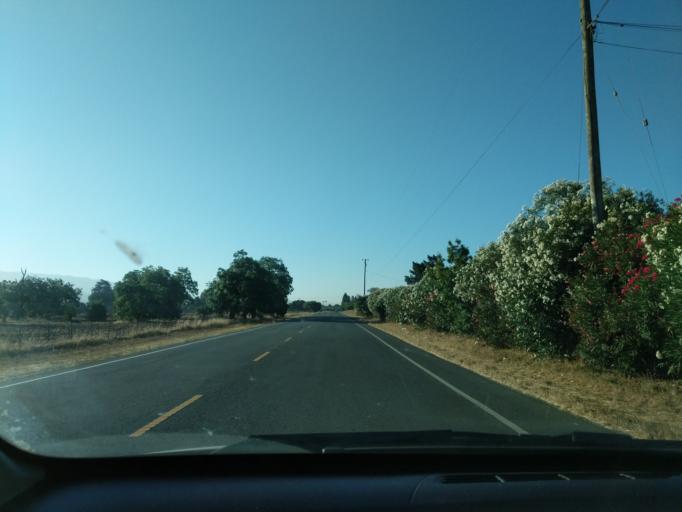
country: US
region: California
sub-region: Santa Clara County
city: Morgan Hill
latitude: 37.1410
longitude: -121.6378
